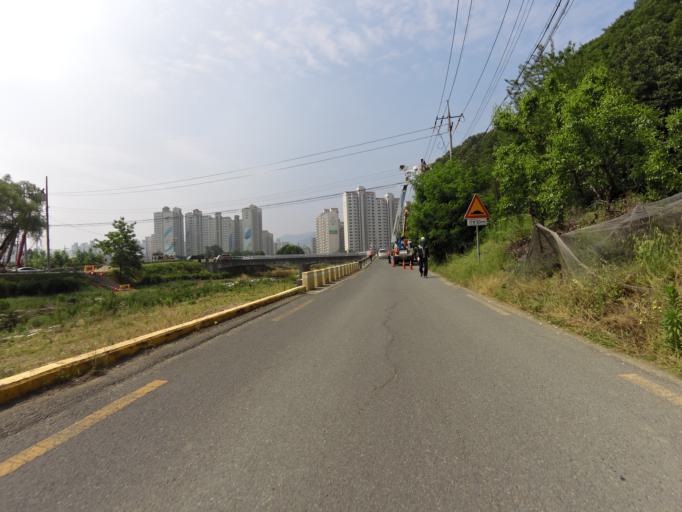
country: KR
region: Gyeongsangbuk-do
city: Gyeongsan-si
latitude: 35.8500
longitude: 128.7073
